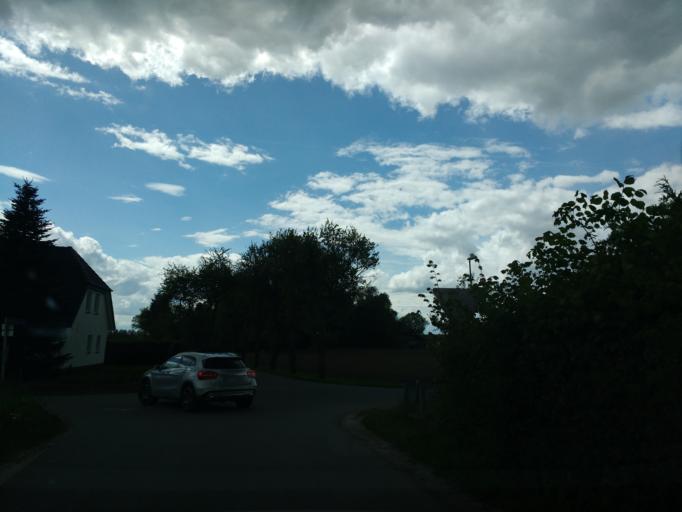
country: DE
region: Schleswig-Holstein
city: Barkelsby
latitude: 54.4951
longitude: 9.8600
